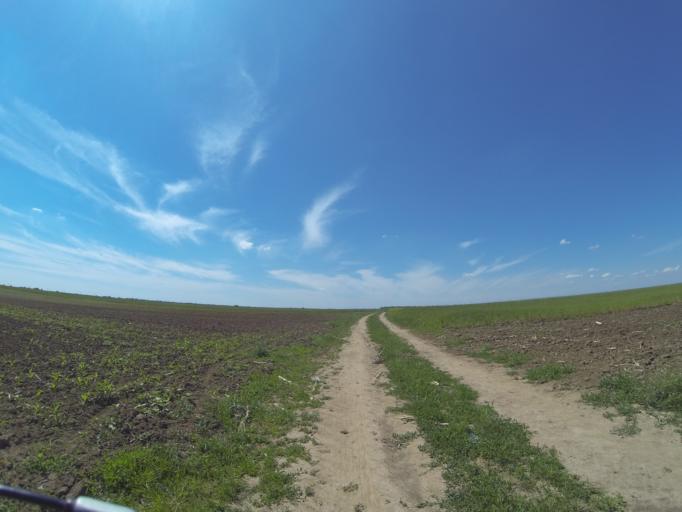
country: RO
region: Dolj
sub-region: Comuna Leu
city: Leu
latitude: 44.2181
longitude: 24.0148
